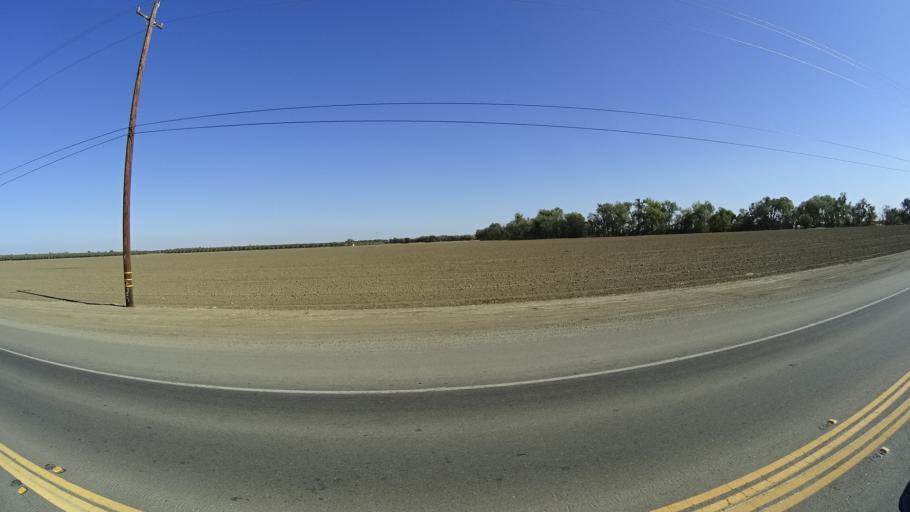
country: US
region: California
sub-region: Yolo County
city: Davis
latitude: 38.5933
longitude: -121.8038
